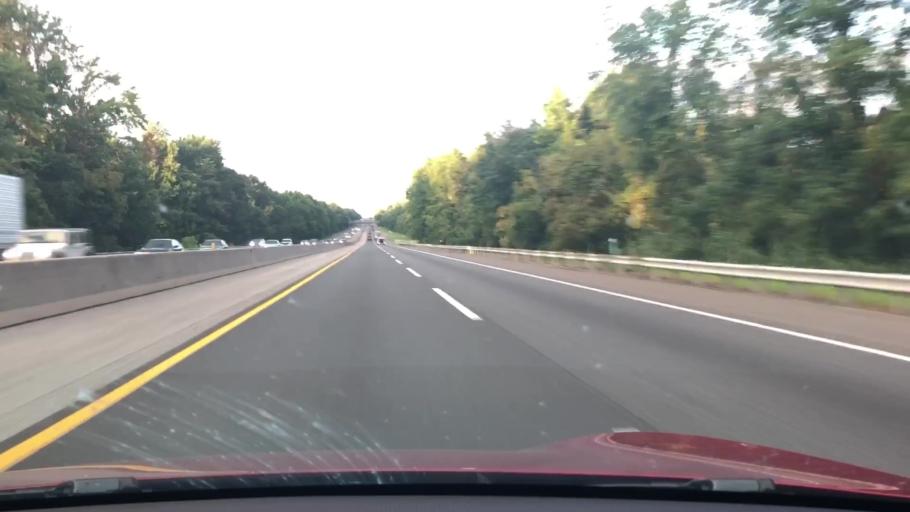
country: US
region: New Jersey
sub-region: Gloucester County
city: Mullica Hill
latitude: 39.7746
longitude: -75.2403
